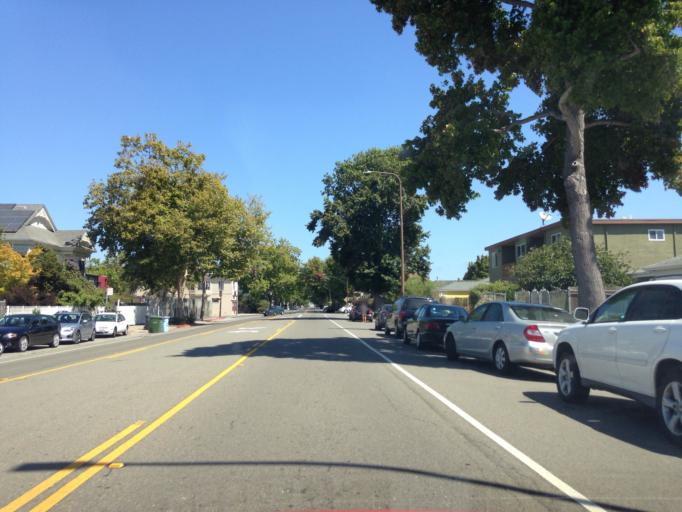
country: US
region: California
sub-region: Alameda County
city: Albany
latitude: 37.8732
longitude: -122.2994
